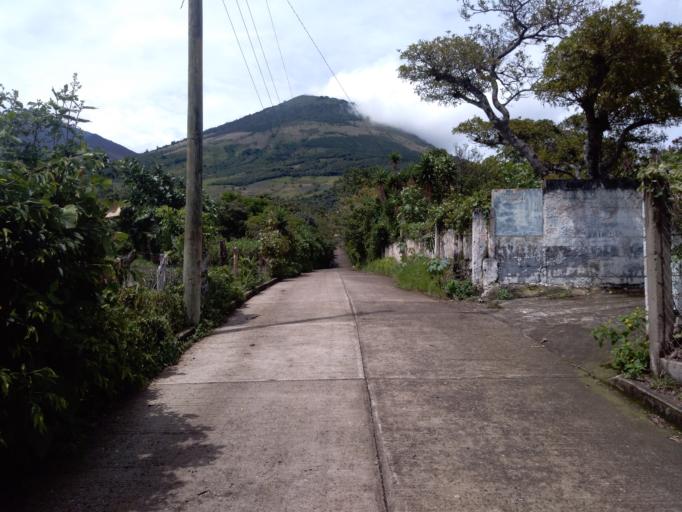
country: GT
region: Escuintla
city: San Vicente Pacaya
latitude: 14.3694
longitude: -90.5657
